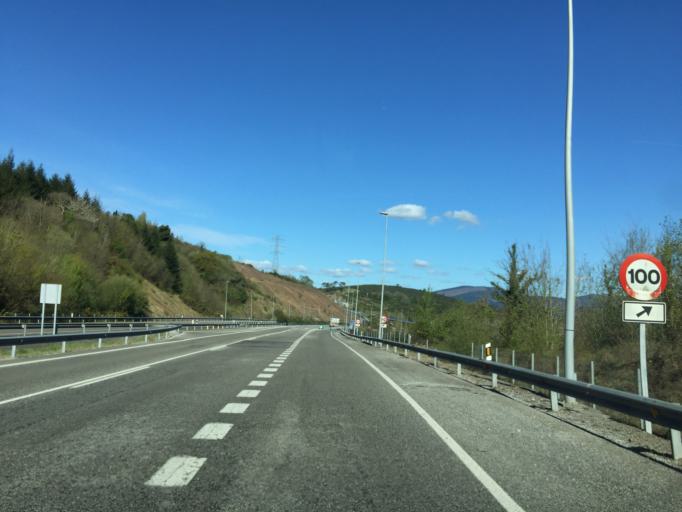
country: ES
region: Asturias
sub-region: Province of Asturias
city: Llanera
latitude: 43.3600
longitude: -5.9455
